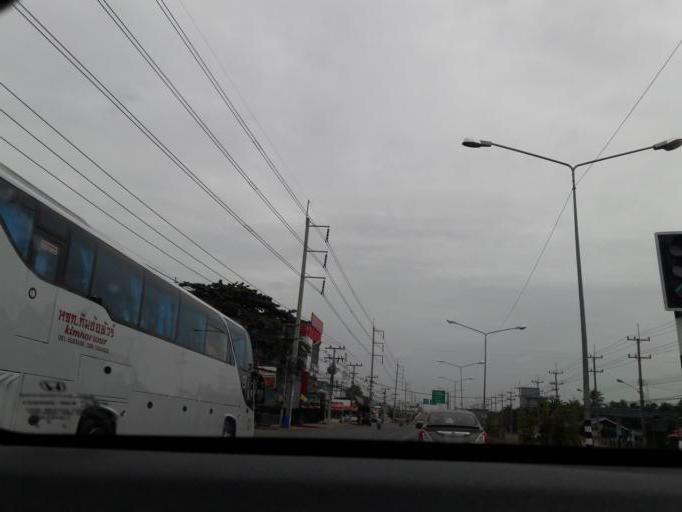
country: TH
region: Ratchaburi
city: Damnoen Saduak
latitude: 13.5234
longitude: 99.9708
